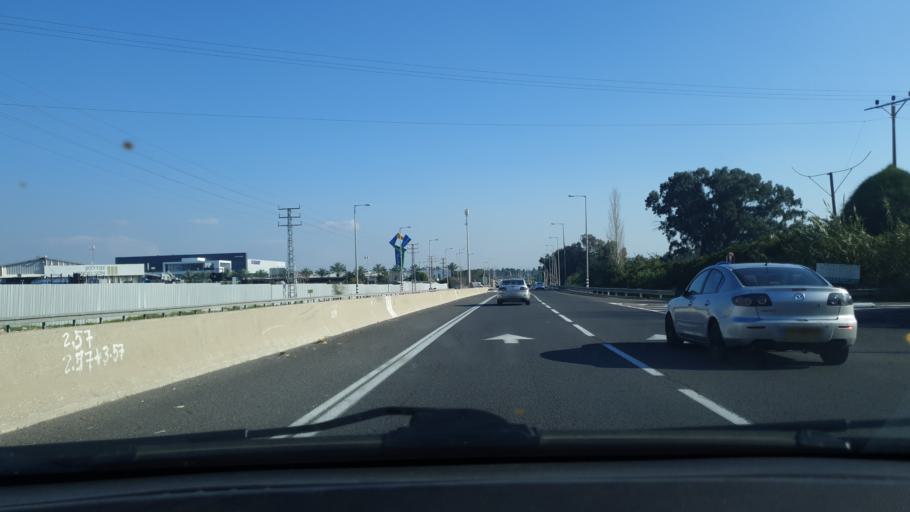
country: IL
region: Central District
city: Kefar Habad
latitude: 31.9659
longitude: 34.8469
